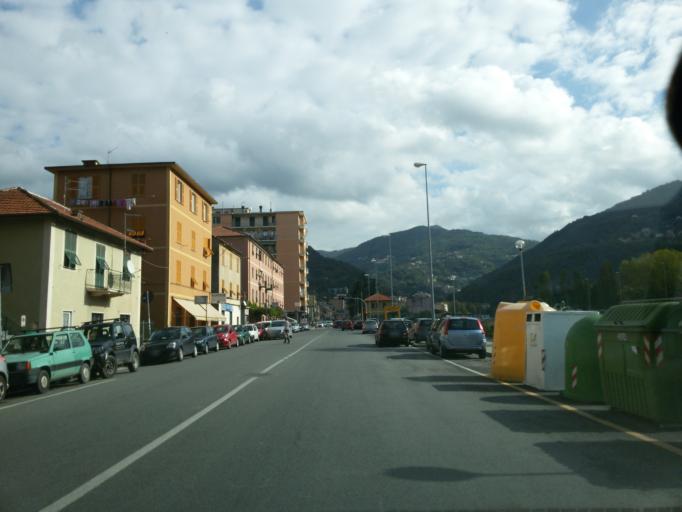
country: IT
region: Liguria
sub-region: Provincia di Genova
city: Piccarello
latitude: 44.4488
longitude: 9.0101
